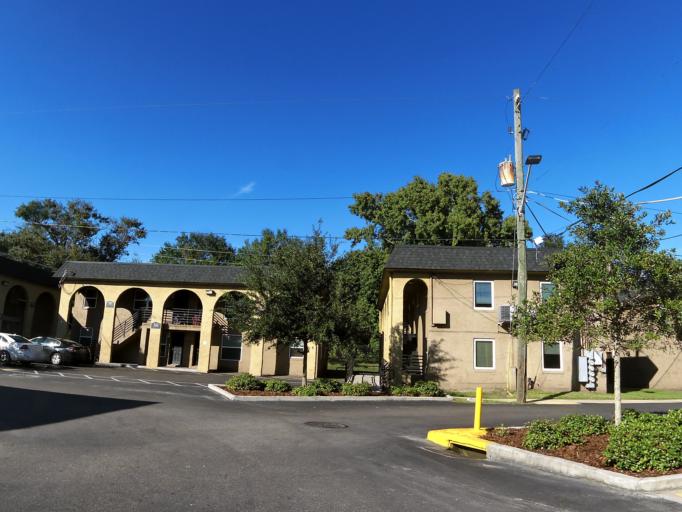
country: US
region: Florida
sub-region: Duval County
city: Jacksonville
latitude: 30.3509
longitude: -81.6655
